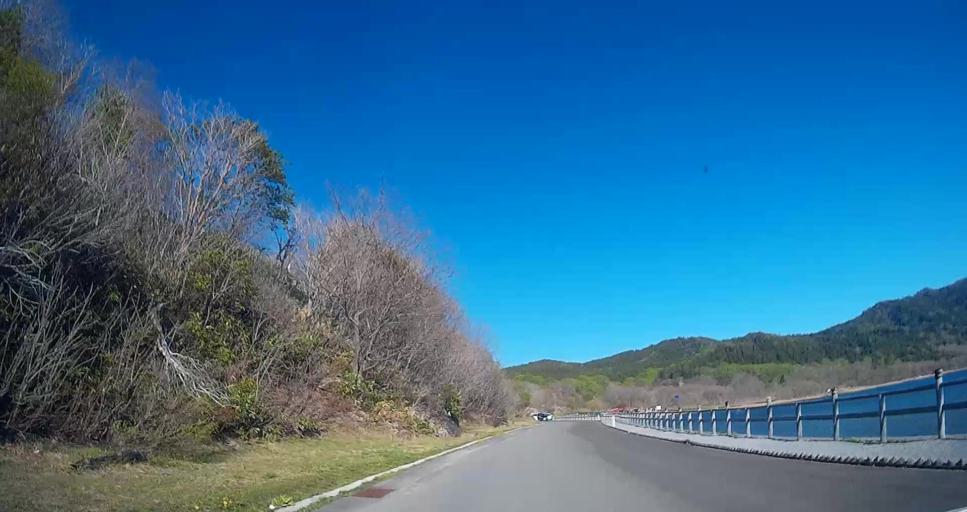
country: JP
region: Aomori
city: Mutsu
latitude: 41.3265
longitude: 141.0935
